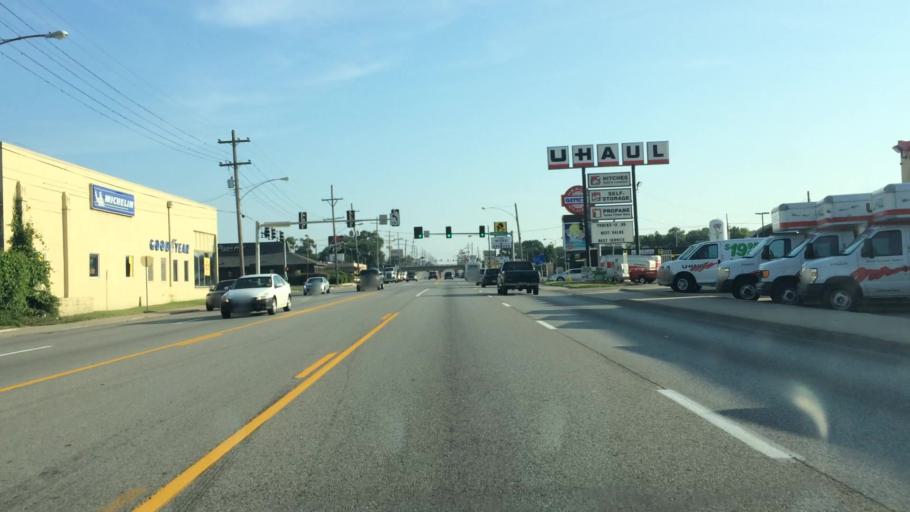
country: US
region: Missouri
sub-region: Greene County
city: Springfield
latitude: 37.2294
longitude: -93.2613
